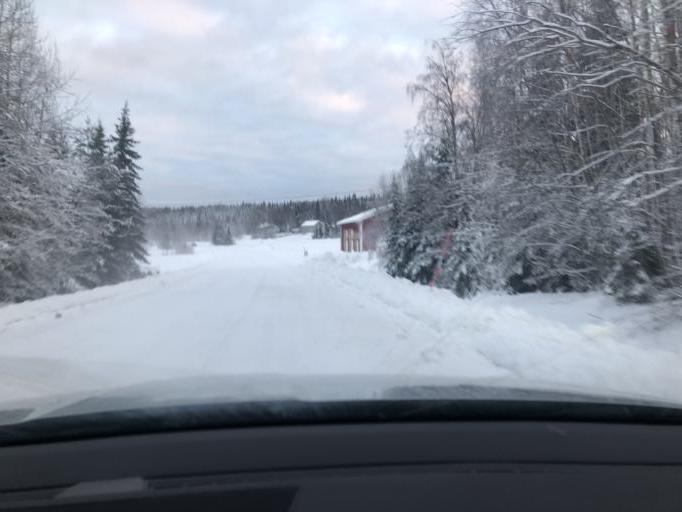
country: SE
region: Vaesternorrland
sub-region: Kramfors Kommun
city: Nordingra
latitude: 62.9990
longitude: 18.2213
